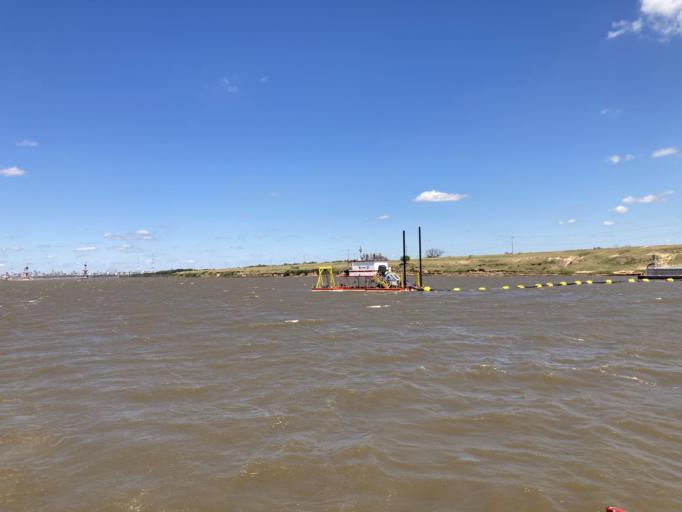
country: PY
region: Central
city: Colonia Mariano Roque Alonso
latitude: -25.2144
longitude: -57.5749
